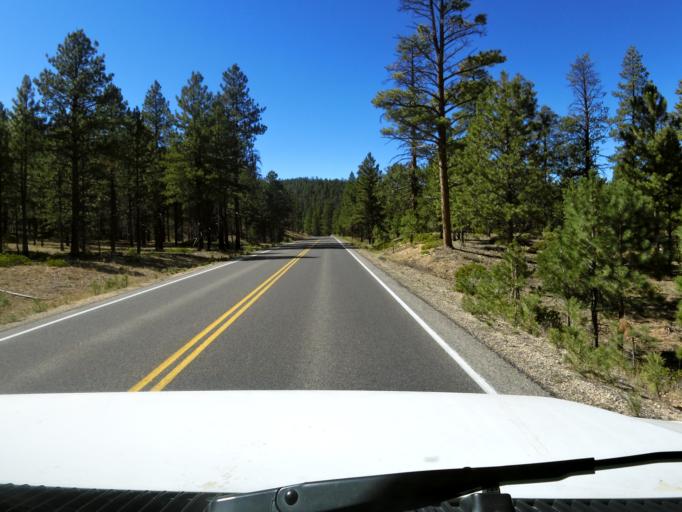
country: US
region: Utah
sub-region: Garfield County
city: Panguitch
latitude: 37.6062
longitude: -112.2016
